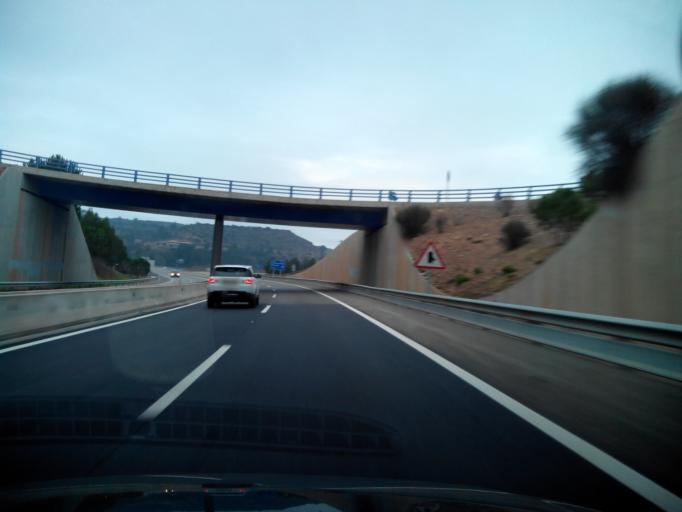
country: ES
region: Catalonia
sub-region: Provincia de Barcelona
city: Balsareny
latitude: 41.8534
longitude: 1.8779
